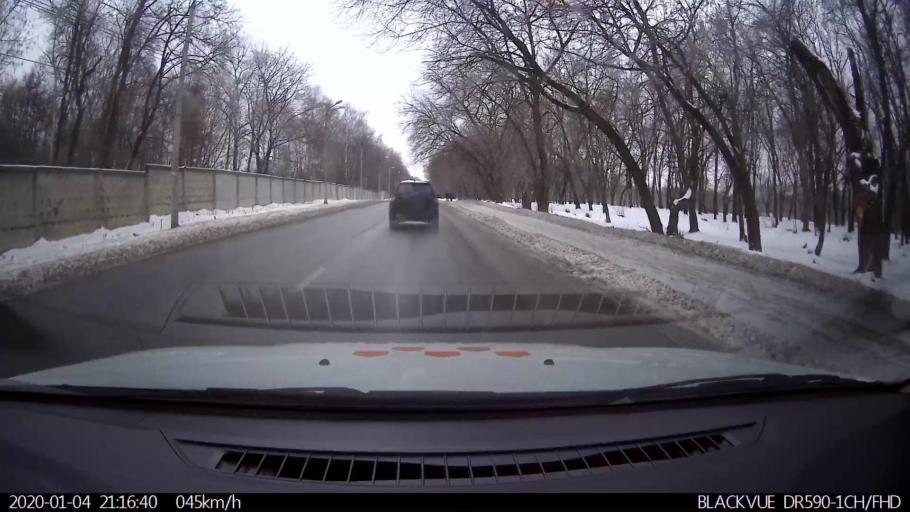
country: RU
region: Nizjnij Novgorod
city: Gorbatovka
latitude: 56.2393
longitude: 43.8493
